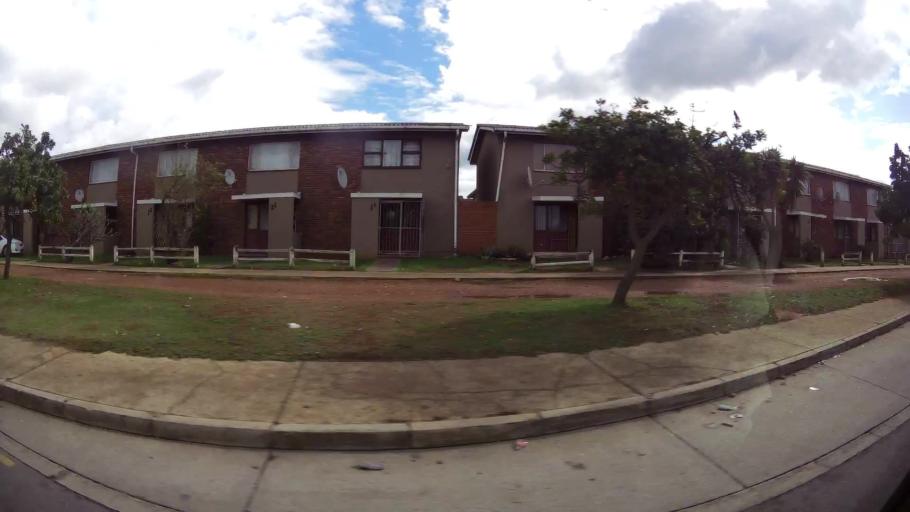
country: ZA
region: Eastern Cape
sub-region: Nelson Mandela Bay Metropolitan Municipality
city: Port Elizabeth
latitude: -33.9254
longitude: 25.5680
